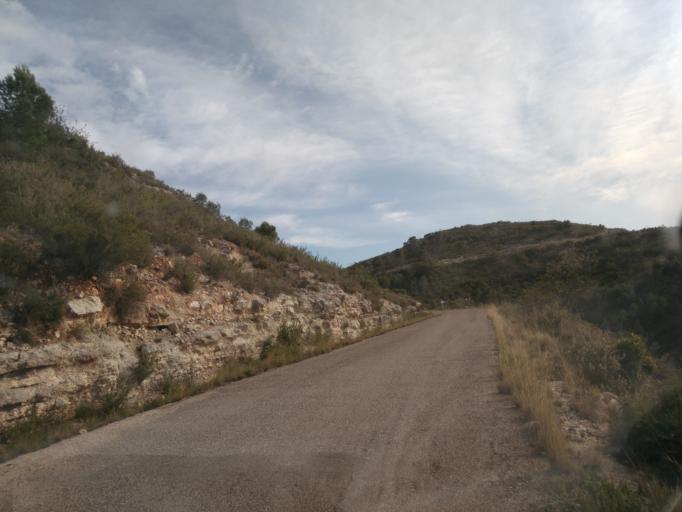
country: ES
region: Valencia
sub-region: Provincia de Valencia
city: Sumacarcer
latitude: 39.1501
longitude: -0.6486
